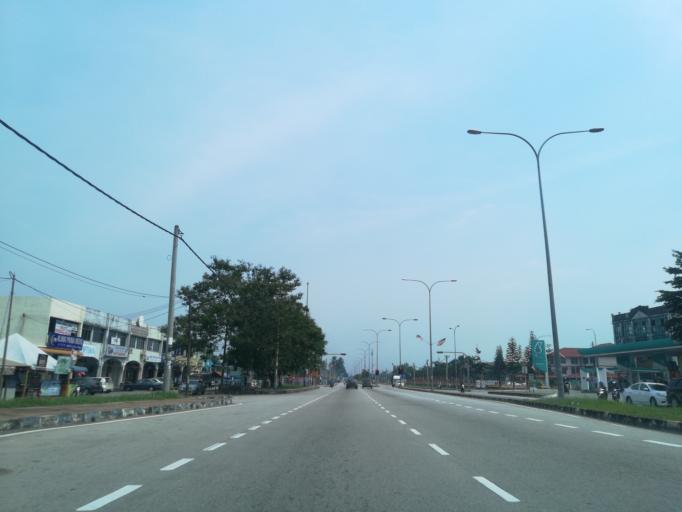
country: MY
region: Kedah
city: Kulim
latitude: 5.3971
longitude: 100.5587
